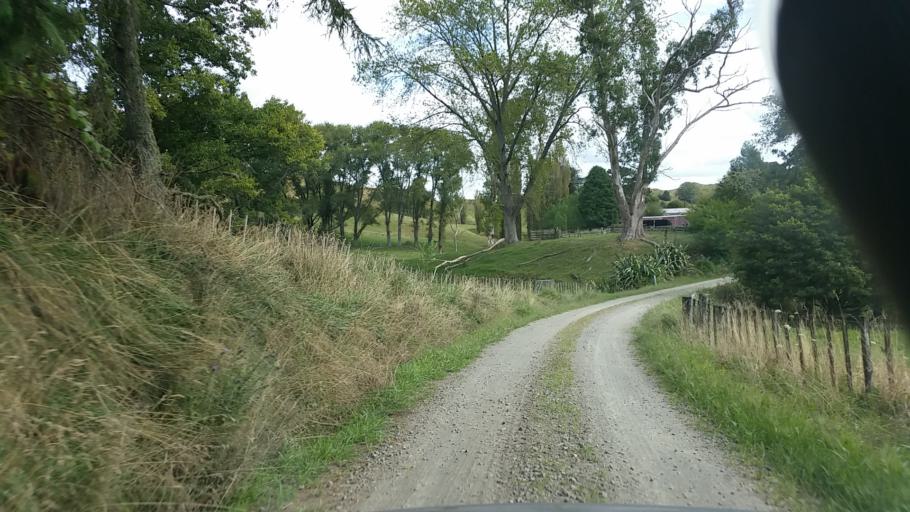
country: NZ
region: Taranaki
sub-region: South Taranaki District
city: Eltham
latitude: -39.2574
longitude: 174.5622
